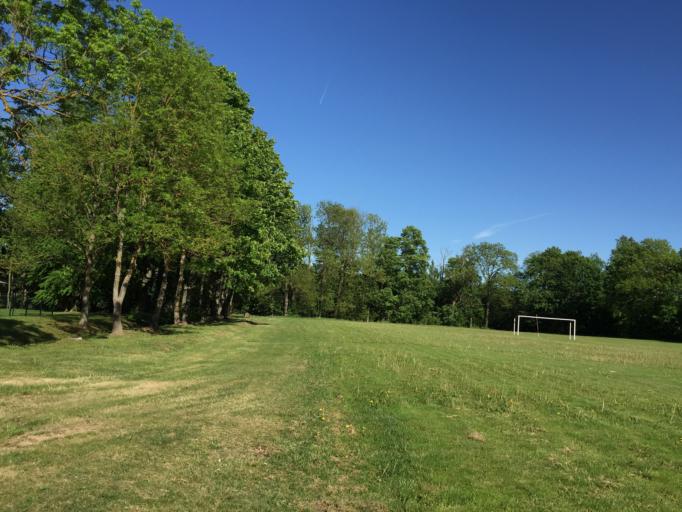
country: LV
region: Jelgava
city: Jelgava
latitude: 56.5209
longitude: 23.7567
